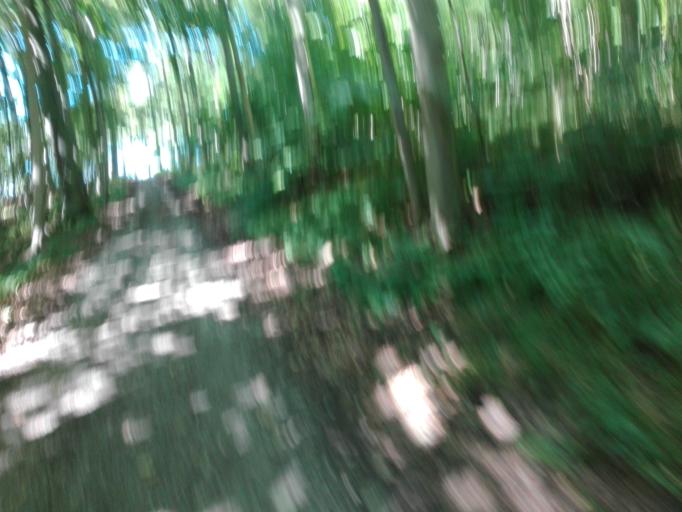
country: DK
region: Central Jutland
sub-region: Odder Kommune
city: Odder
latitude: 55.9594
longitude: 10.1405
